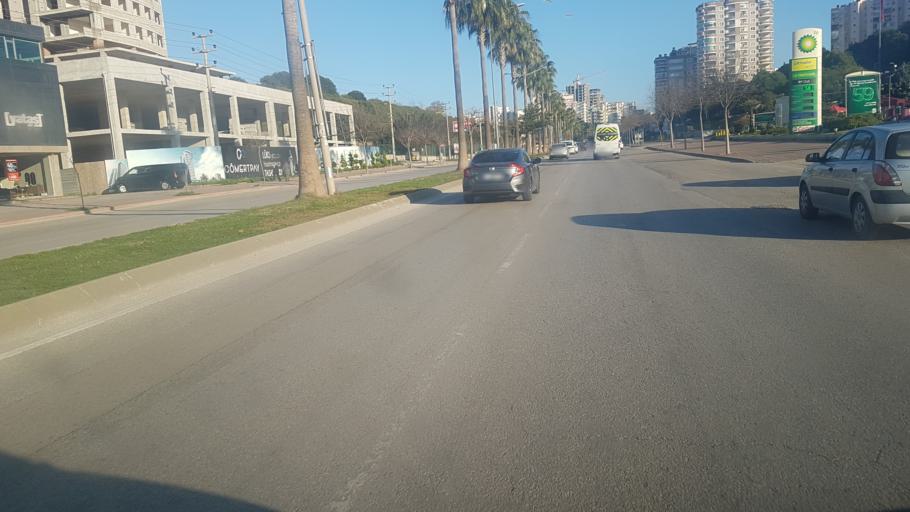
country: TR
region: Adana
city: Seyhan
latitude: 37.0440
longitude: 35.2553
